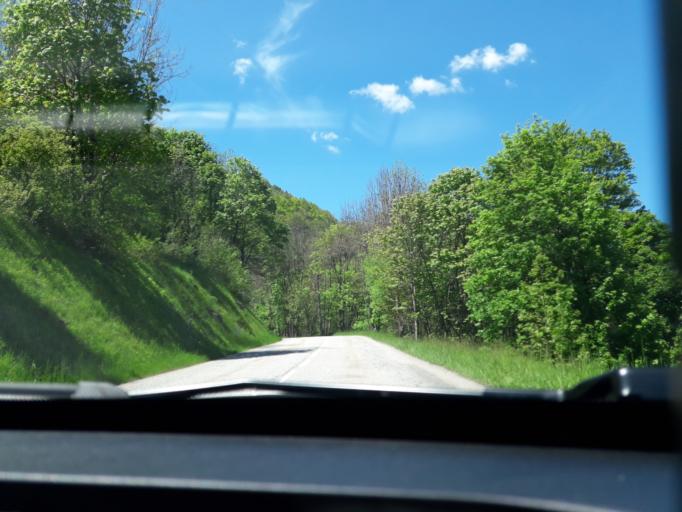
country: FR
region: Rhone-Alpes
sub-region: Departement de la Savoie
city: Saint-Martin-de-Belleville
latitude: 45.4108
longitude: 6.4894
